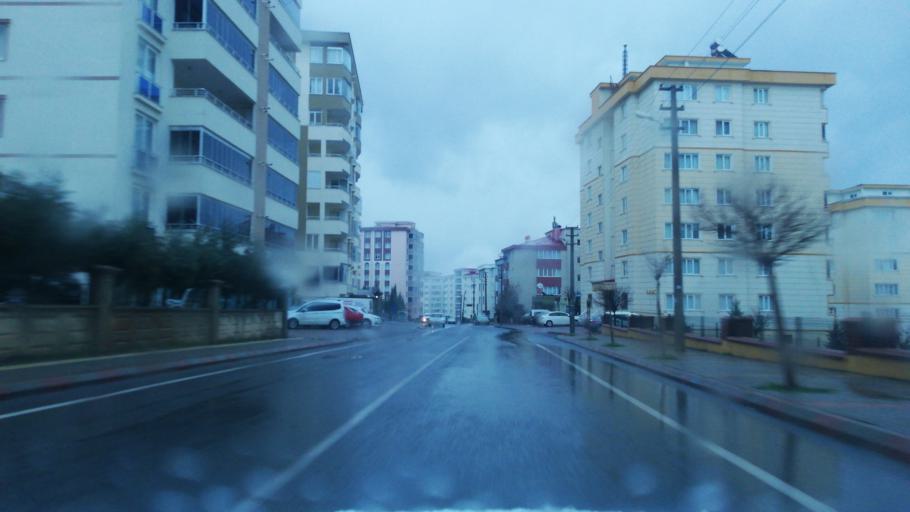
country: TR
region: Kahramanmaras
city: Kahramanmaras
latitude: 37.5994
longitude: 36.8862
